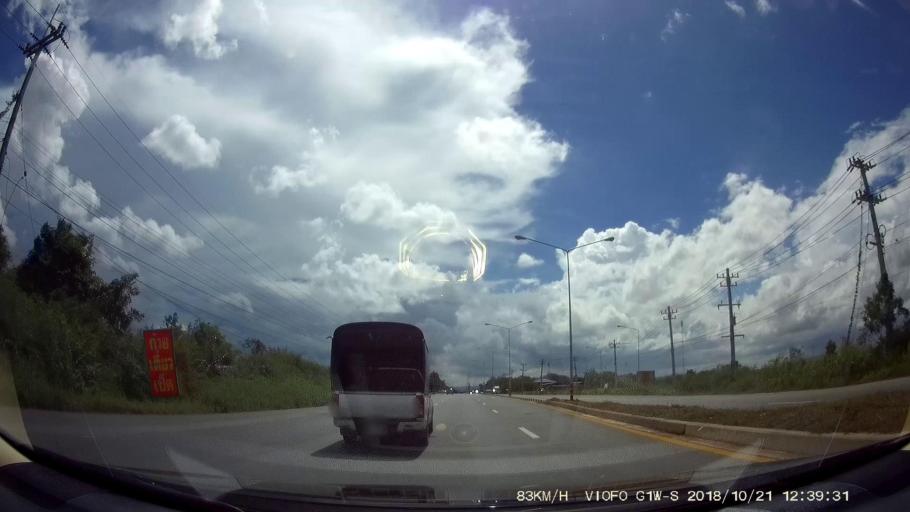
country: TH
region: Nakhon Ratchasima
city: Amphoe Sikhiu
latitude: 15.0380
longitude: 101.7004
